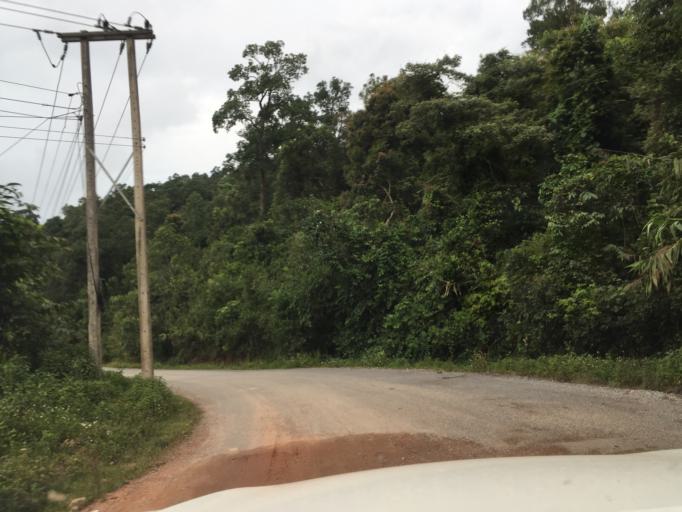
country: LA
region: Phongsali
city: Phongsali
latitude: 21.3283
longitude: 102.0533
